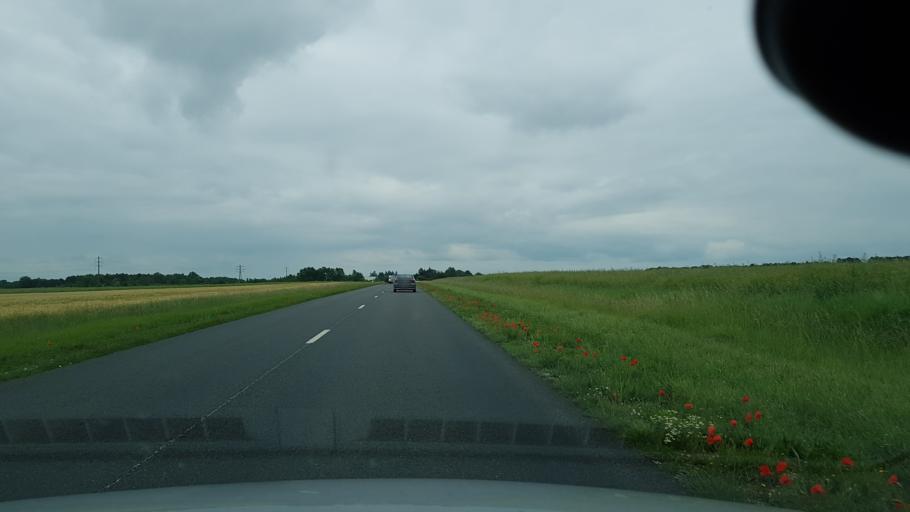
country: FR
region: Centre
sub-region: Departement du Loir-et-Cher
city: Chatillon-sur-Cher
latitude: 47.2980
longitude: 1.5170
